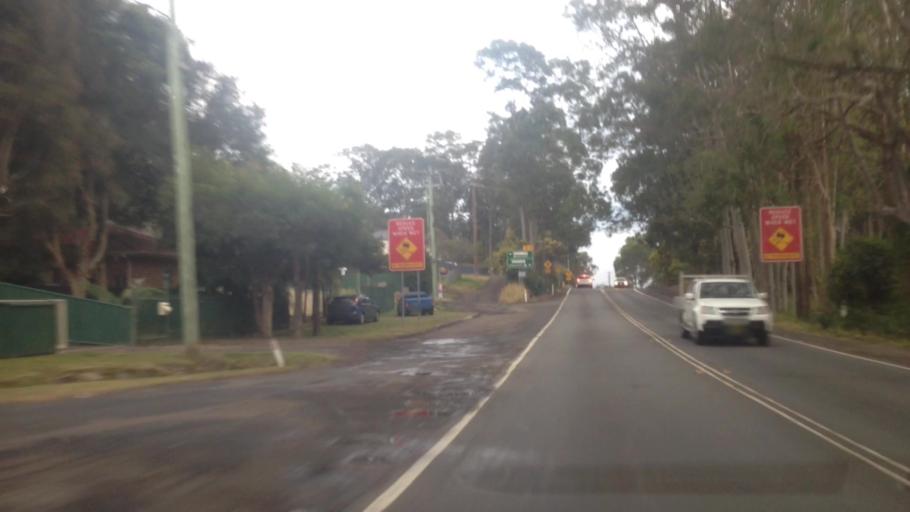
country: AU
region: New South Wales
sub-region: Wyong Shire
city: Jilliby
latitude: -33.2699
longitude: 151.4314
